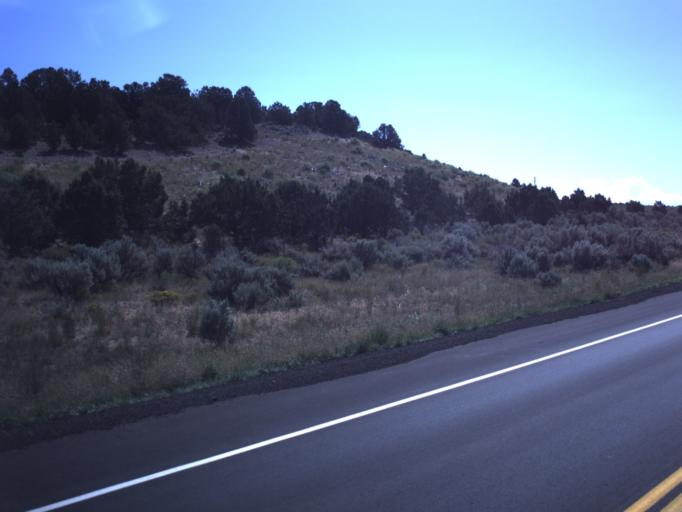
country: US
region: Utah
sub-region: Utah County
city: Genola
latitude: 39.9735
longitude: -112.2581
